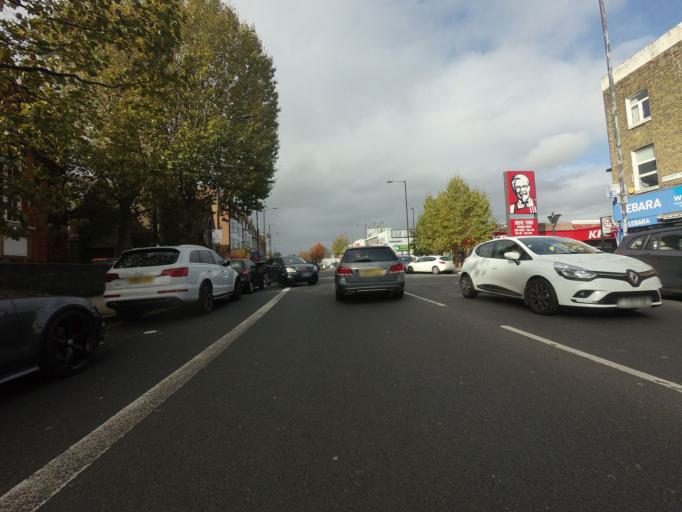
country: GB
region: England
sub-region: Greater London
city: Camberwell
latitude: 51.4820
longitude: -0.0621
